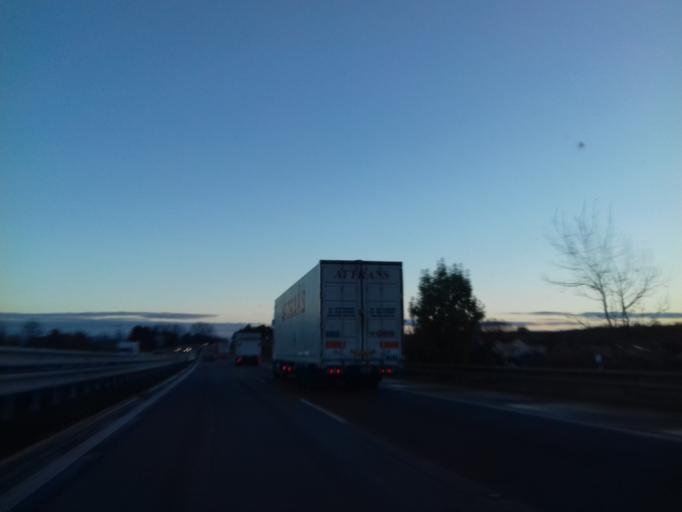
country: CZ
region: South Moravian
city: Rousinov
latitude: 49.1933
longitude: 16.8868
